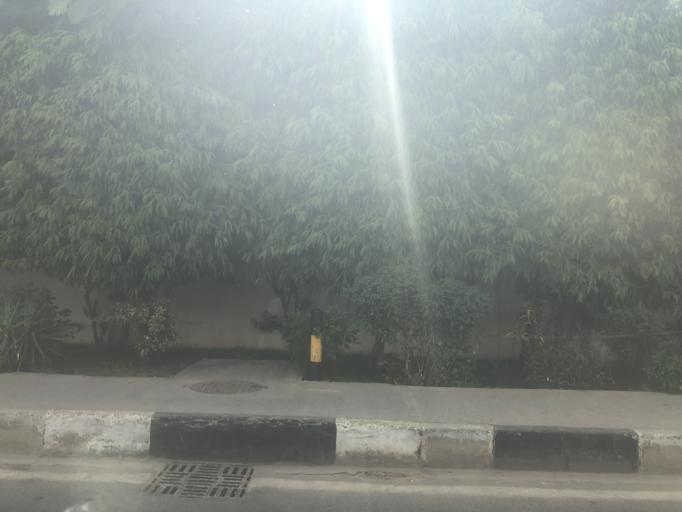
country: SN
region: Dakar
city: Mermoz Boabab
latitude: 14.7376
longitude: -17.5095
